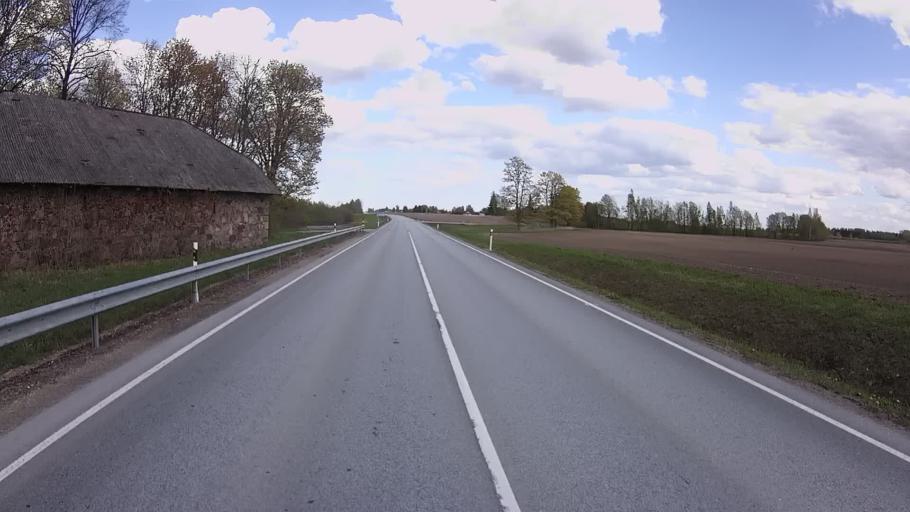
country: EE
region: Jogevamaa
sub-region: Mustvee linn
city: Mustvee
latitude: 58.8234
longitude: 26.6940
